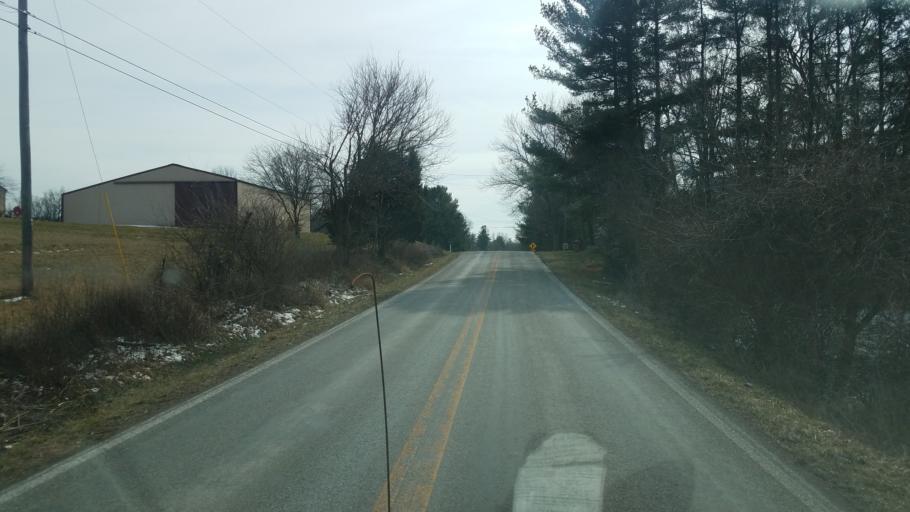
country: US
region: Ohio
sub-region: Delaware County
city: Delaware
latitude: 40.3513
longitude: -83.0323
